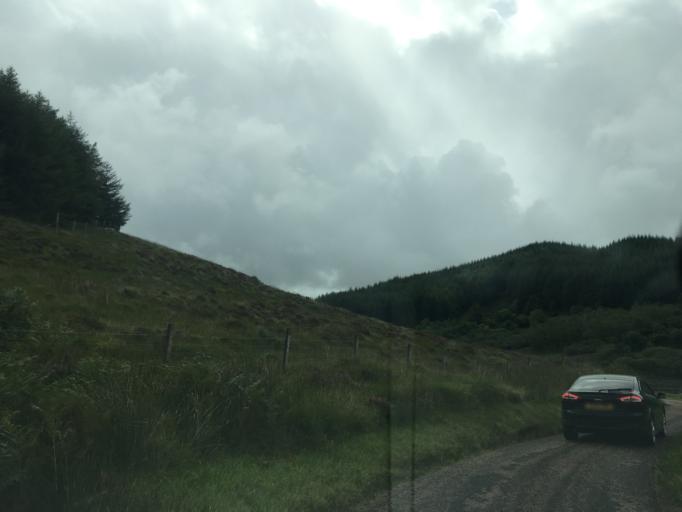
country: GB
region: Scotland
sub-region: Argyll and Bute
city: Oban
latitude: 56.2535
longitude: -5.4422
